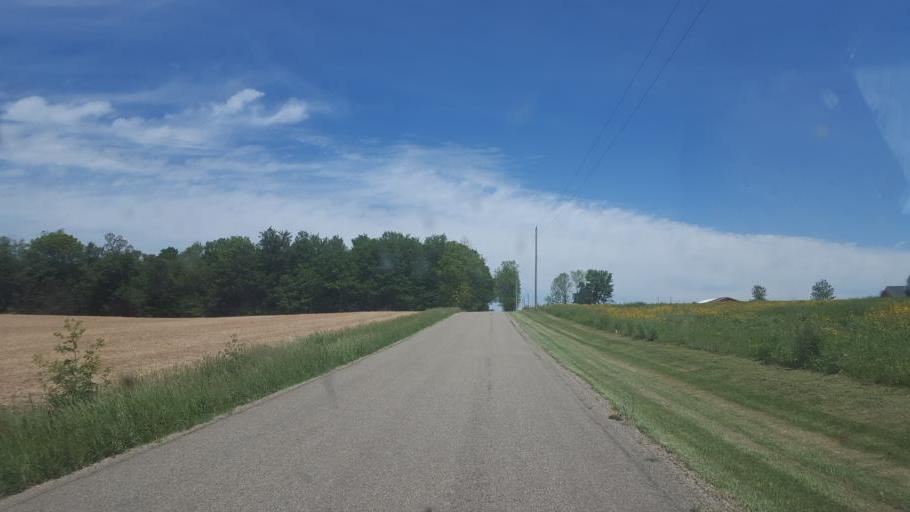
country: US
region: Ohio
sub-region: Knox County
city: Gambier
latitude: 40.3557
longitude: -82.3106
